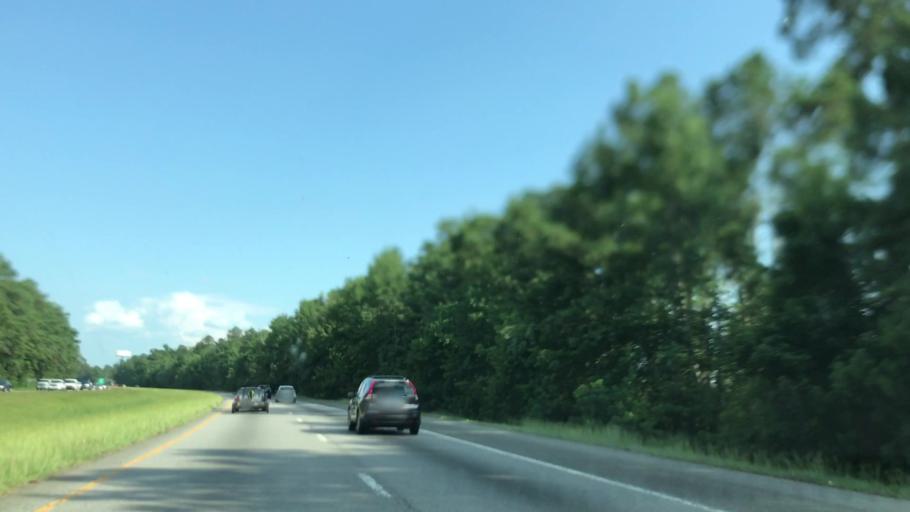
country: US
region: South Carolina
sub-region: Orangeburg County
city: Brookdale
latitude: 33.4764
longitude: -80.7536
